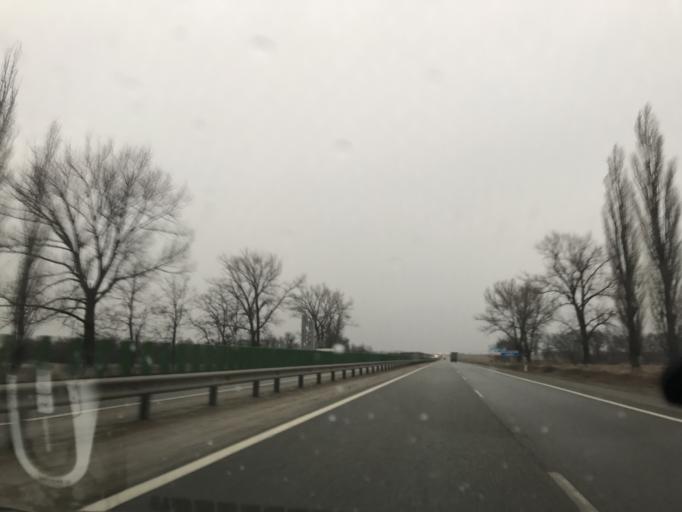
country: RU
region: Krasnodarskiy
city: Pavlovskaya
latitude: 46.2306
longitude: 39.8315
